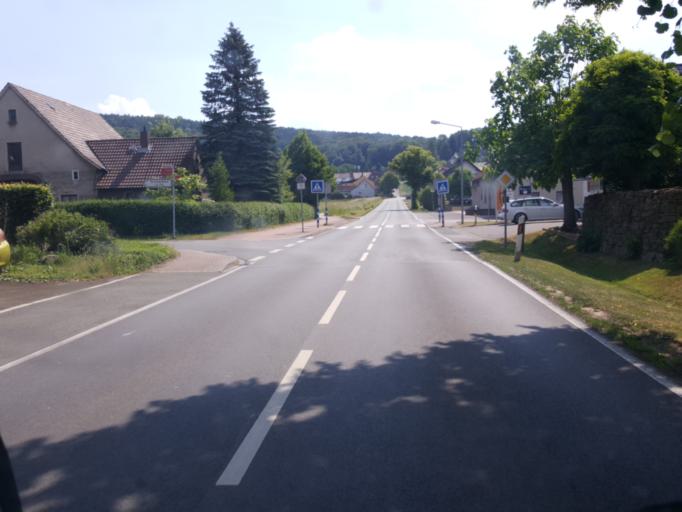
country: DE
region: North Rhine-Westphalia
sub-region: Regierungsbezirk Detmold
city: Hille
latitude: 52.2765
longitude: 8.7837
